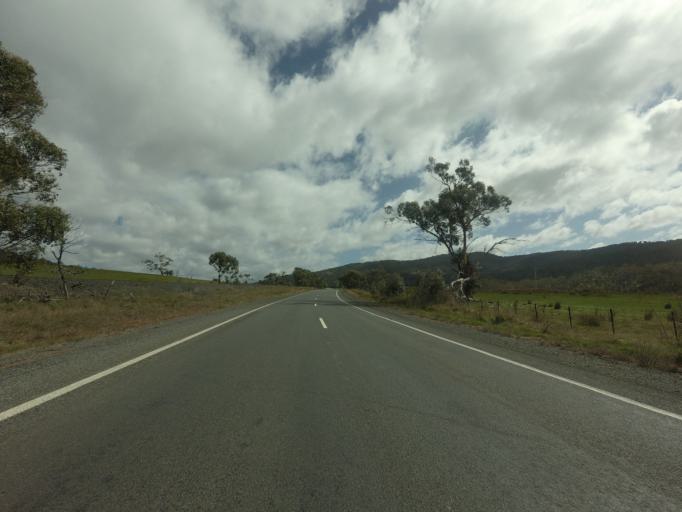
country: AU
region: Tasmania
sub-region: Northern Midlands
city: Evandale
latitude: -41.8122
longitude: 147.6073
